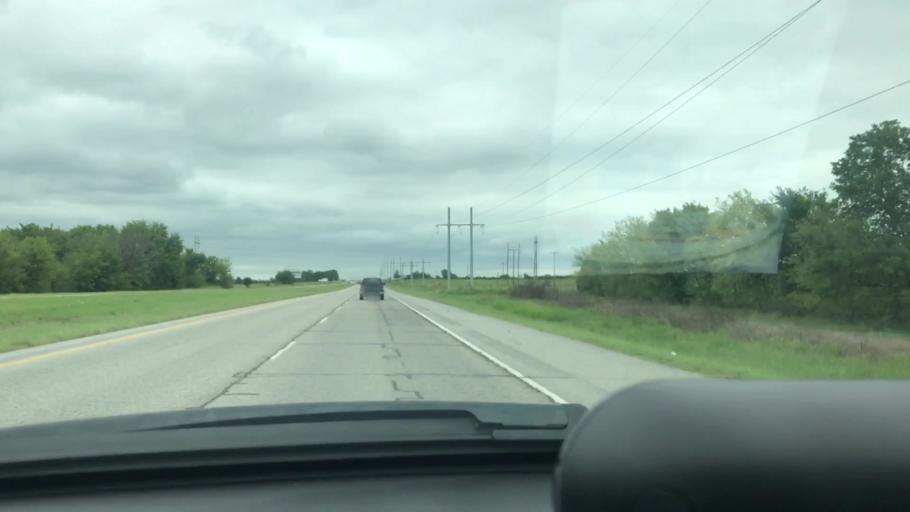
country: US
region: Oklahoma
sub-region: Wagoner County
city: Wagoner
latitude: 36.0048
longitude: -95.3688
